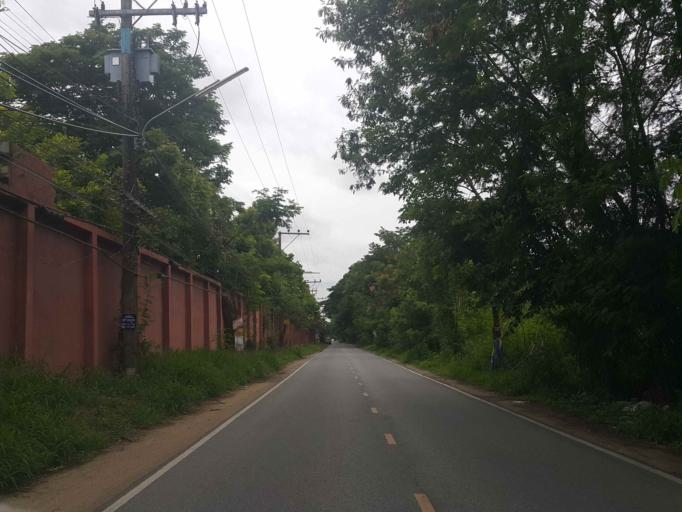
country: TH
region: Chiang Mai
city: Chiang Mai
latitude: 18.7639
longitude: 98.9902
